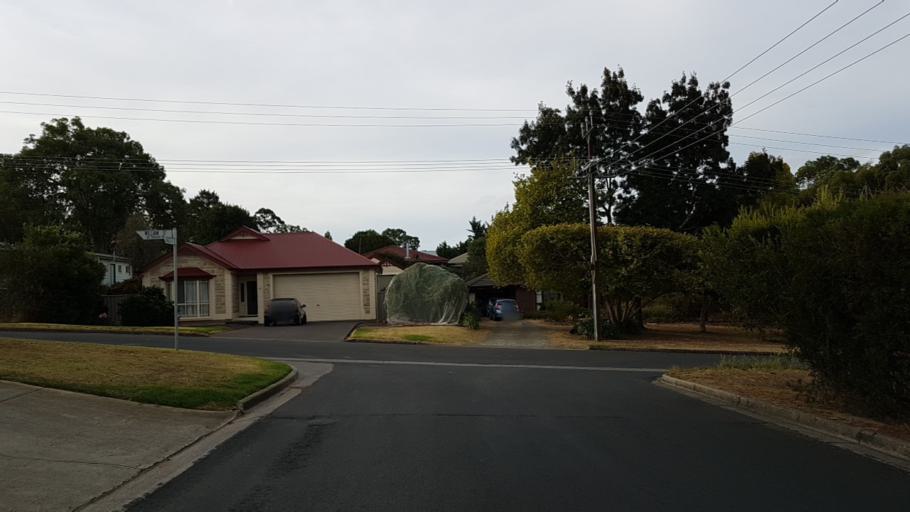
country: AU
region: South Australia
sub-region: Mount Barker
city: Nairne
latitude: -35.0291
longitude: 138.9096
